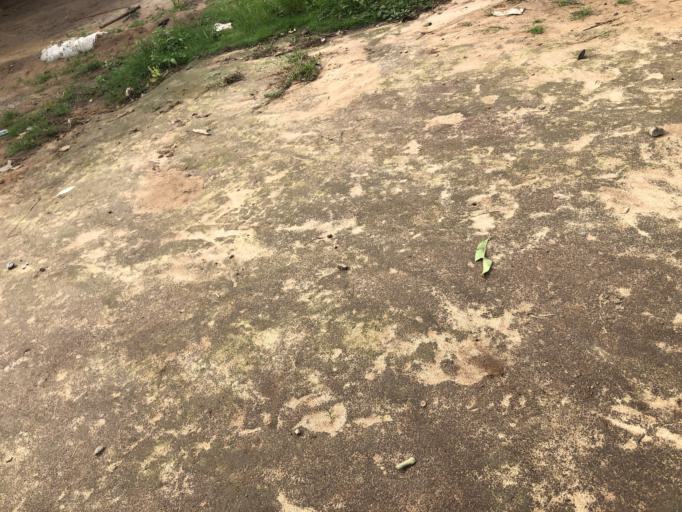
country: SL
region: Northern Province
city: Bumbuna
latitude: 9.0485
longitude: -11.7503
